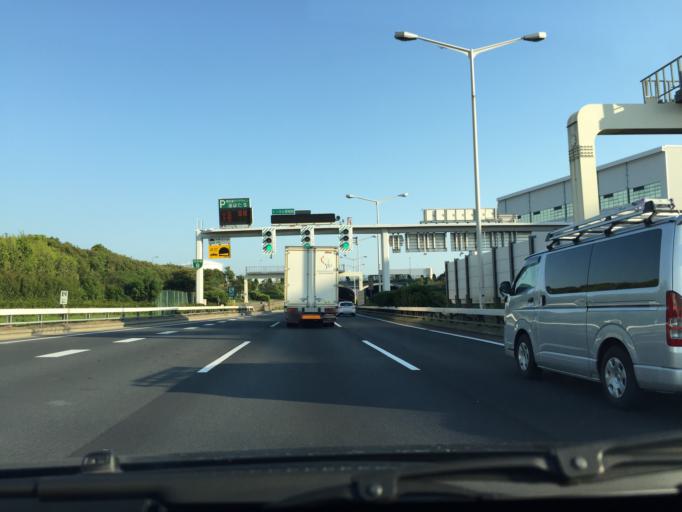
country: JP
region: Kanagawa
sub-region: Kawasaki-shi
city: Kawasaki
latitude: 35.5379
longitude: 139.7946
